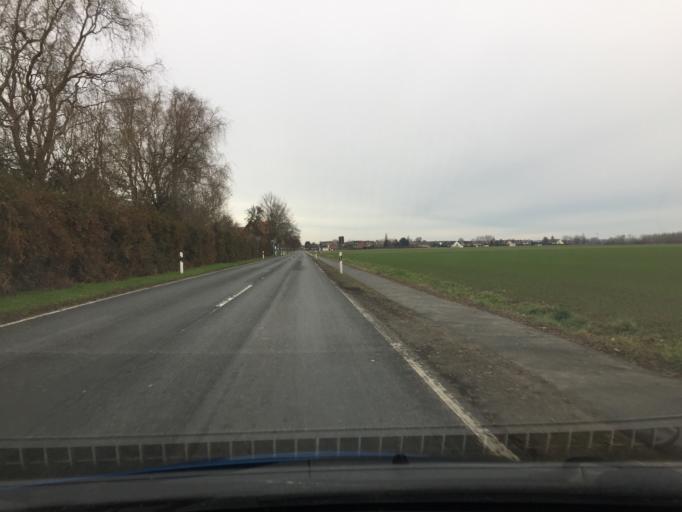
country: DE
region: Lower Saxony
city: Pattensen
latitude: 52.2796
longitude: 9.7661
